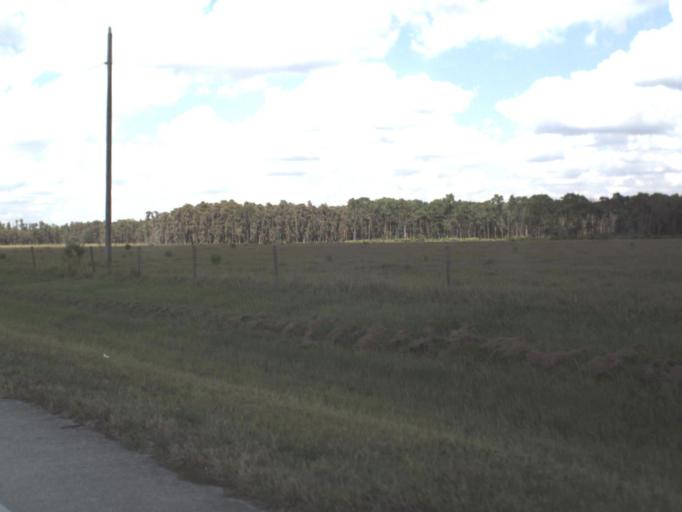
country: US
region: Florida
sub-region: Highlands County
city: Sebring
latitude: 27.4400
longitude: -81.6111
